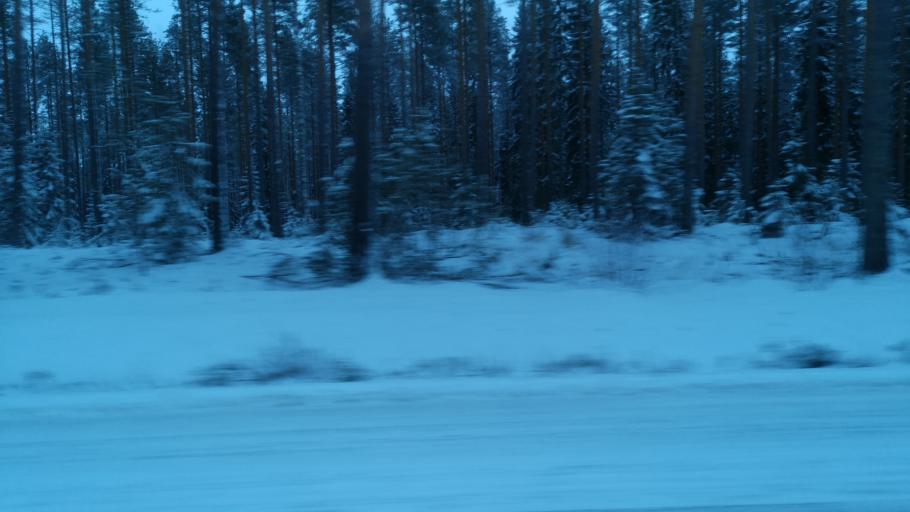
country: FI
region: Southern Savonia
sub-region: Savonlinna
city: Savonlinna
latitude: 61.9672
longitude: 28.8183
